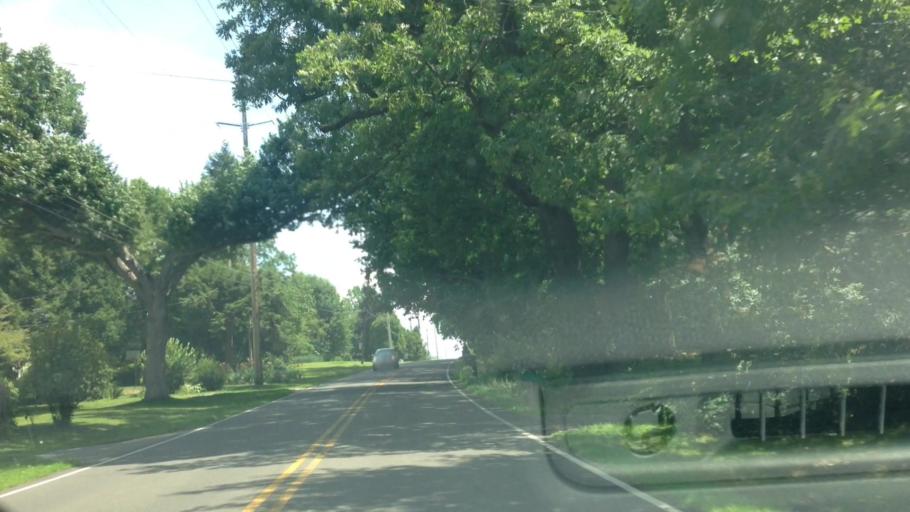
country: US
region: Ohio
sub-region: Summit County
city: Manchester
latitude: 40.9523
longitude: -81.5730
